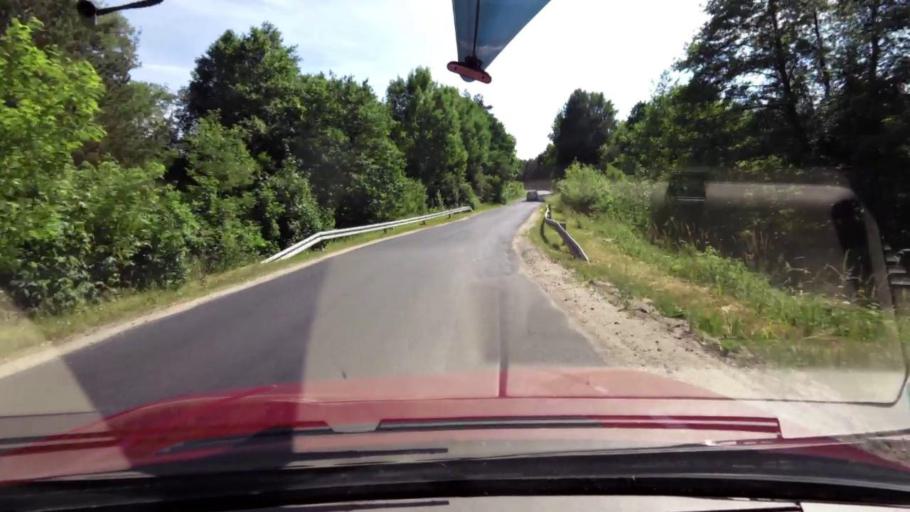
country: PL
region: Pomeranian Voivodeship
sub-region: Powiat slupski
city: Kepice
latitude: 54.2890
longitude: 16.9606
